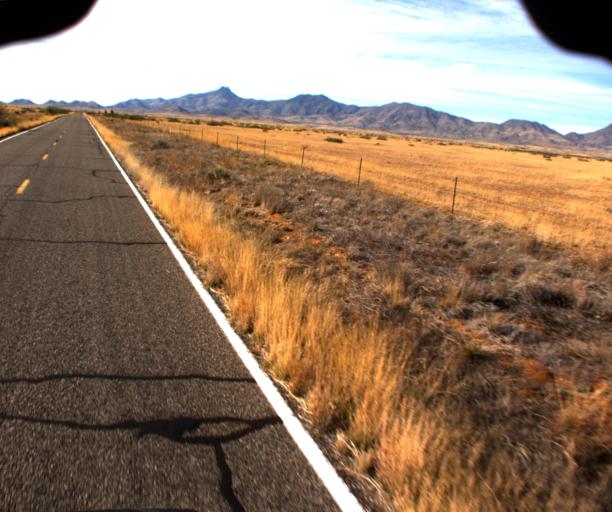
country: US
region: Arizona
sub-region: Cochise County
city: Willcox
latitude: 32.0867
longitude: -109.5274
